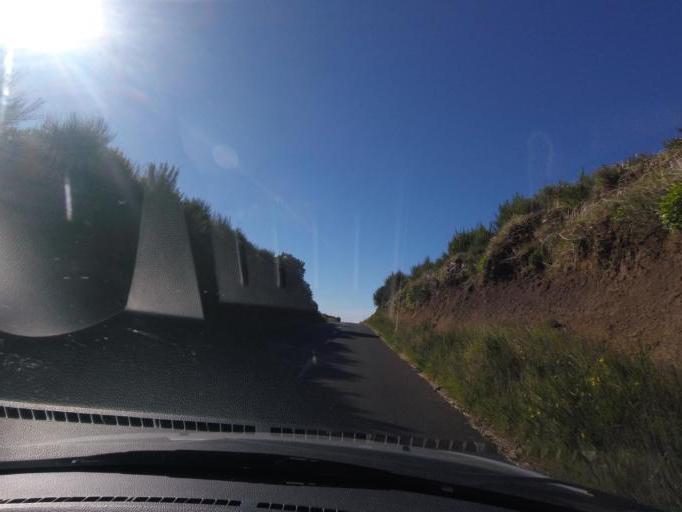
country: PT
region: Madeira
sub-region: Funchal
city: Nossa Senhora do Monte
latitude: 32.7151
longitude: -16.9015
